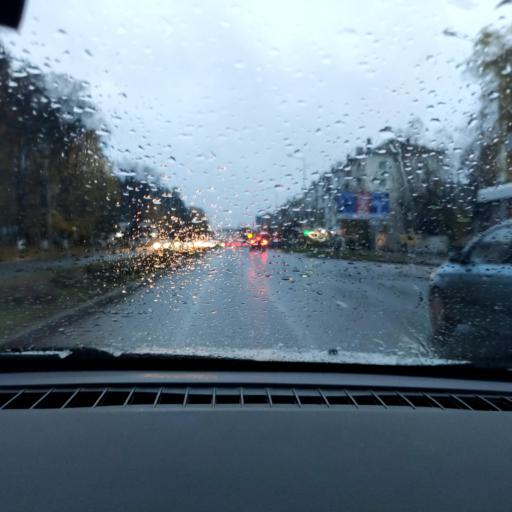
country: RU
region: Perm
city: Kultayevo
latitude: 58.0125
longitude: 55.9715
